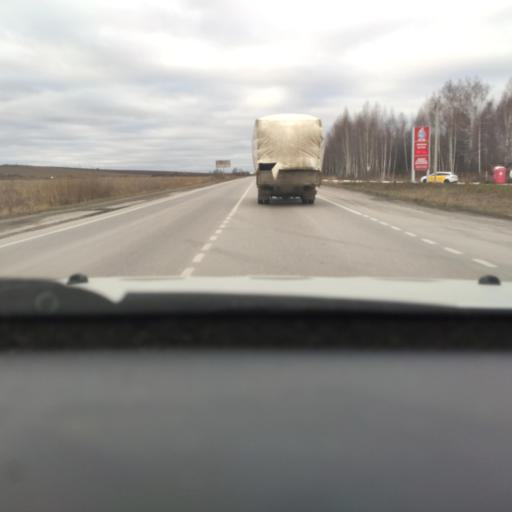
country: RU
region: Perm
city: Froly
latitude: 57.8979
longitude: 56.2412
